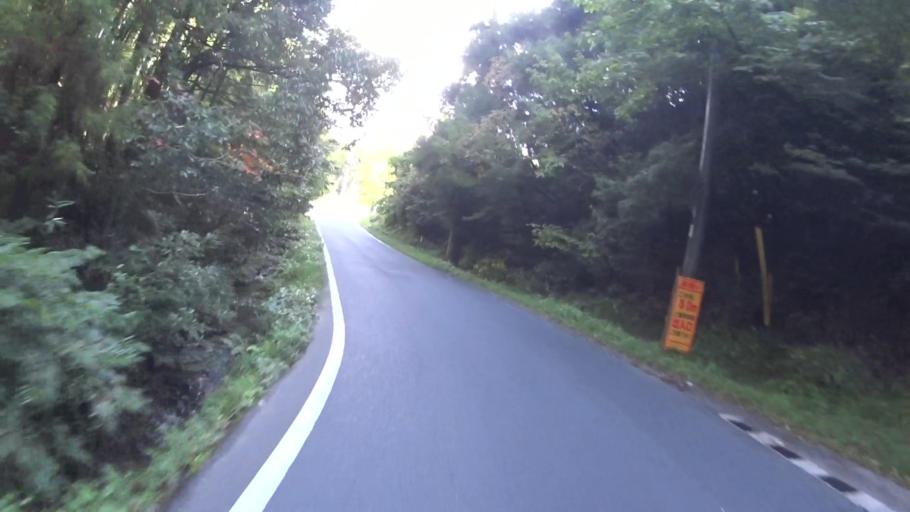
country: JP
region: Kyoto
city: Miyazu
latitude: 35.5817
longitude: 135.1600
